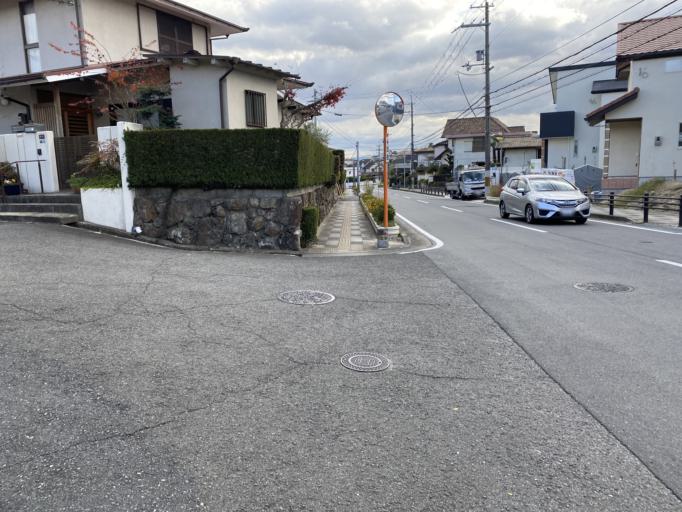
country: JP
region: Nara
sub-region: Ikoma-shi
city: Ikoma
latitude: 34.7135
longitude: 135.7456
